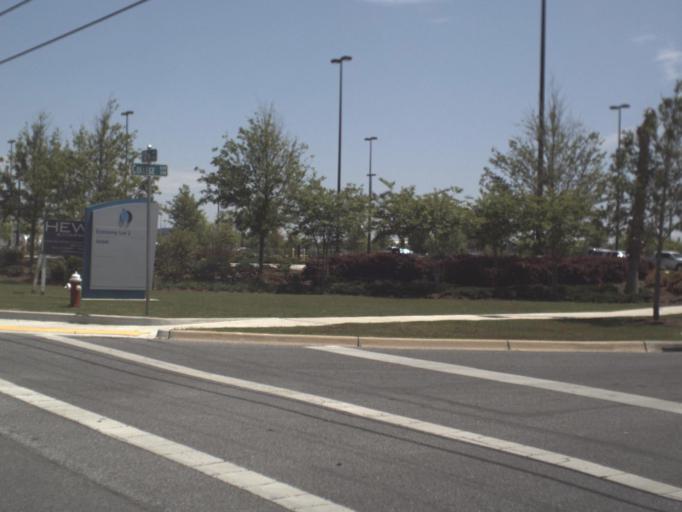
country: US
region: Florida
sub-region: Escambia County
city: Ferry Pass
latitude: 30.4773
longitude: -87.1975
